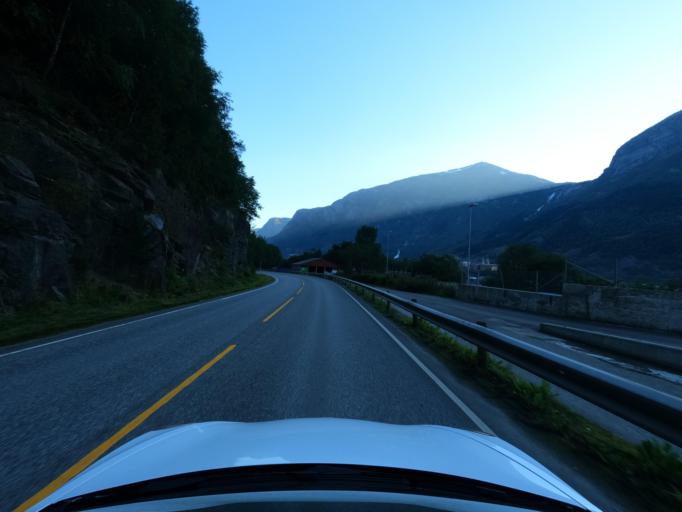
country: NO
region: Hordaland
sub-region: Odda
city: Odda
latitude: 60.0987
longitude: 6.5477
